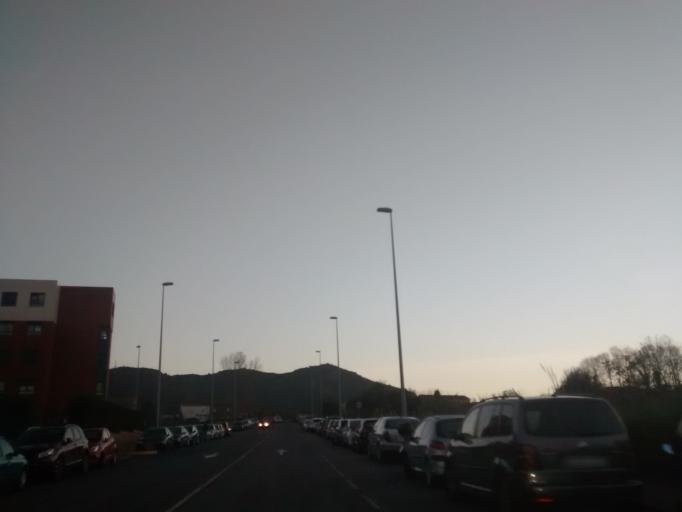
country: ES
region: Cantabria
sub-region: Provincia de Cantabria
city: Santa Cruz de Bezana
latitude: 43.4568
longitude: -3.8587
